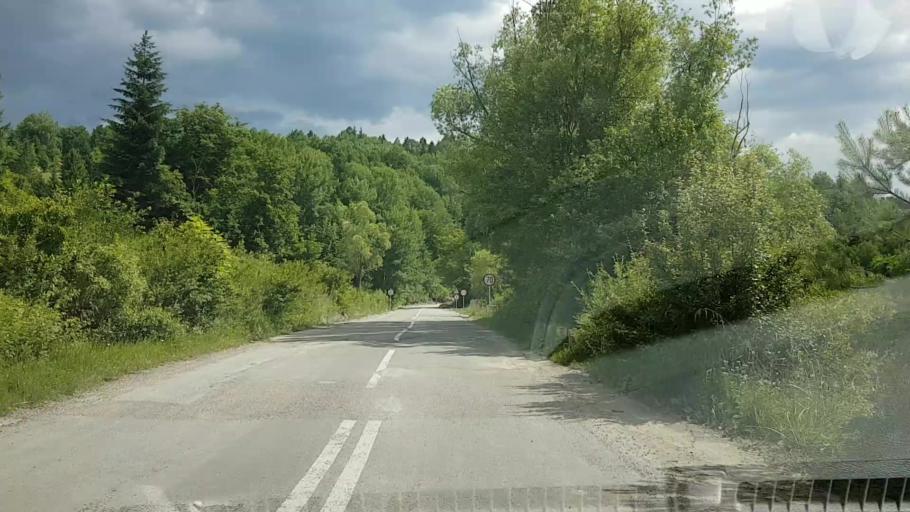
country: RO
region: Neamt
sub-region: Comuna Poiana Teiului
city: Poiana Teiului
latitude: 47.0808
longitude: 25.9678
